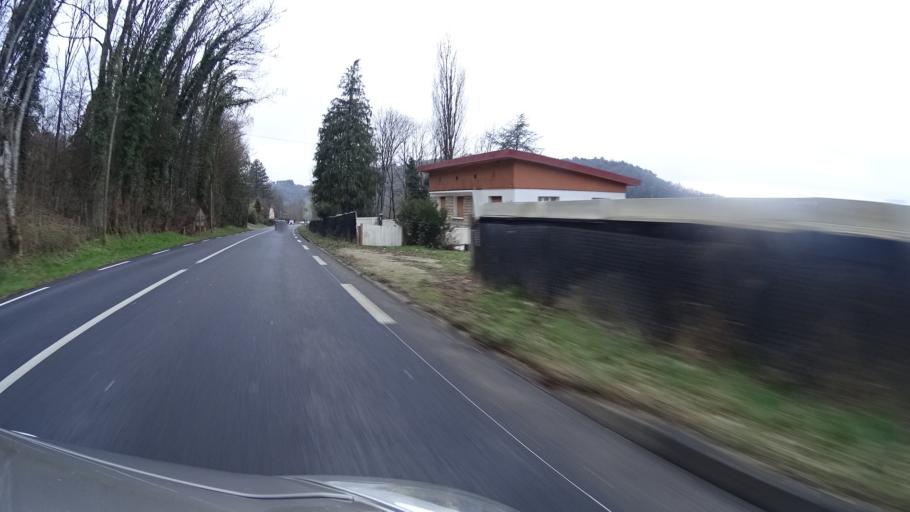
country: FR
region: Franche-Comte
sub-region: Departement du Doubs
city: Morre
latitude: 47.2235
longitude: 6.0697
